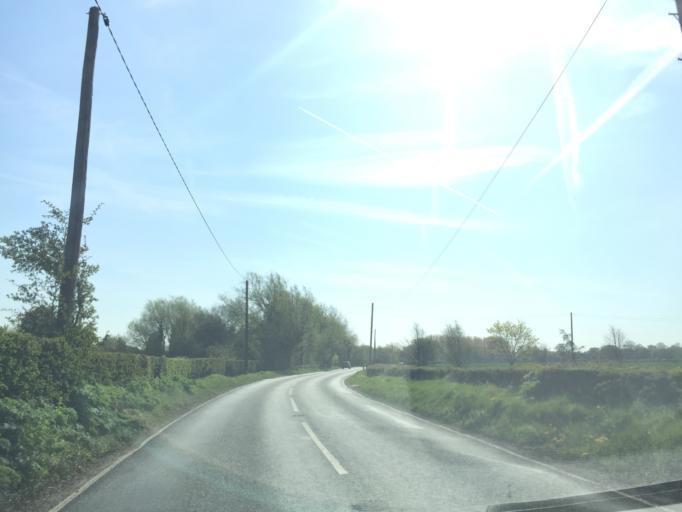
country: GB
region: England
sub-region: Greater London
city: Collier Row
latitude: 51.6570
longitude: 0.1641
